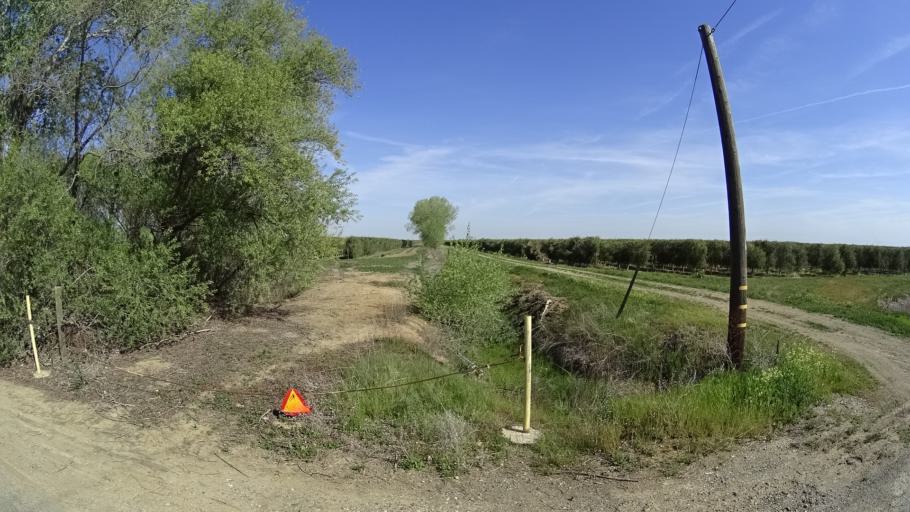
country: US
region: California
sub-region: Glenn County
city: Willows
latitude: 39.6114
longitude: -122.2316
